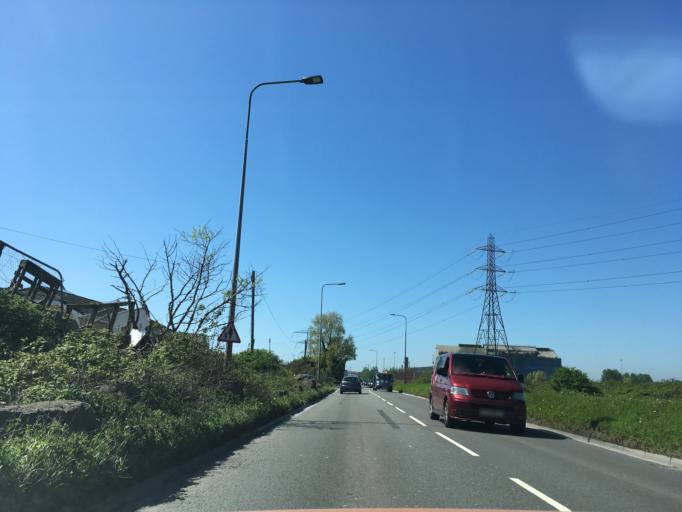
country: GB
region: Wales
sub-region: Cardiff
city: Cardiff
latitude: 51.4853
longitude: -3.1259
